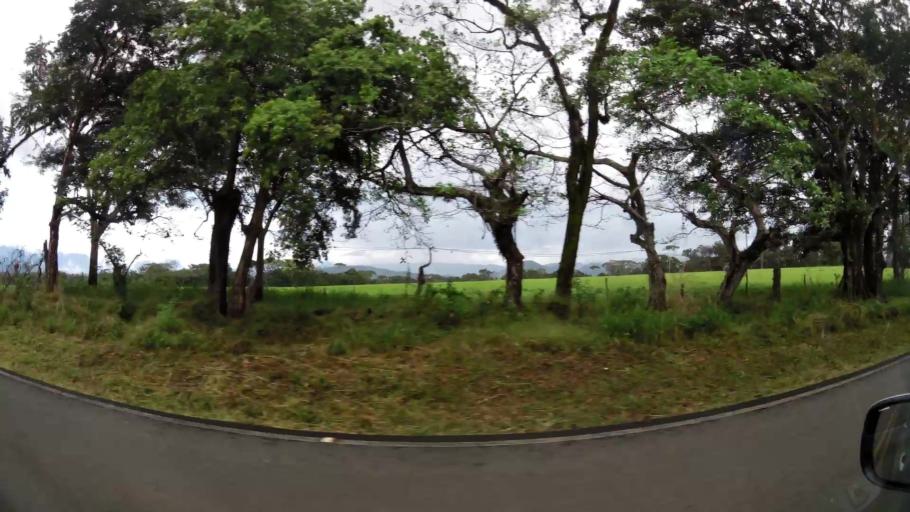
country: CR
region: Puntarenas
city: Esparza
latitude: 9.9901
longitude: -84.6304
